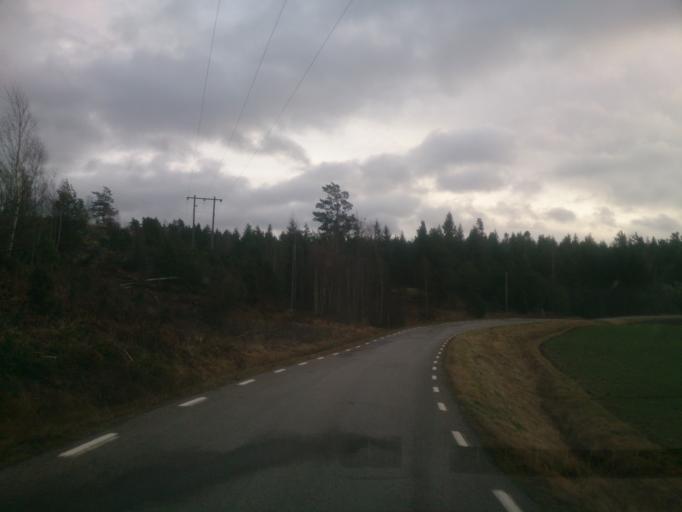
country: SE
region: OEstergoetland
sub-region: Norrkopings Kommun
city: Krokek
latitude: 58.5192
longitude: 16.6027
